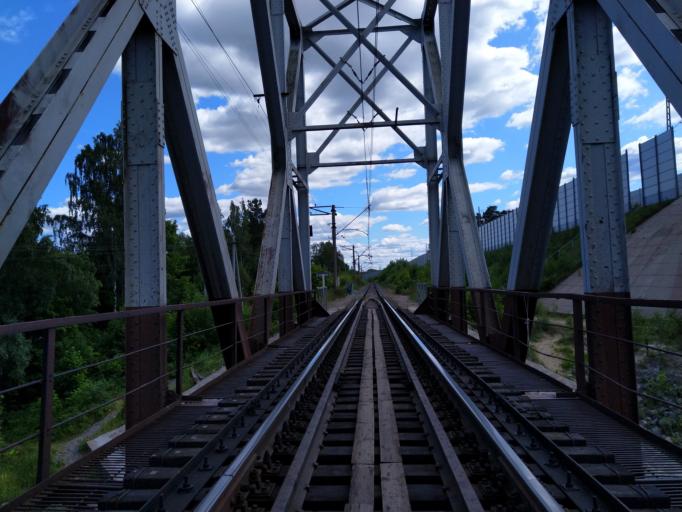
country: RU
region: Leningrad
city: Sapernoye
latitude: 60.6819
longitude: 30.0093
